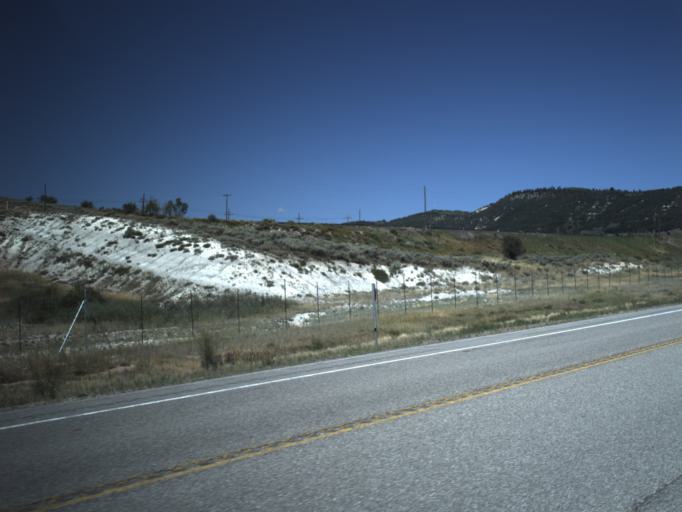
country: US
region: Utah
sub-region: Carbon County
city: Helper
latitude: 39.9178
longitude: -111.0642
